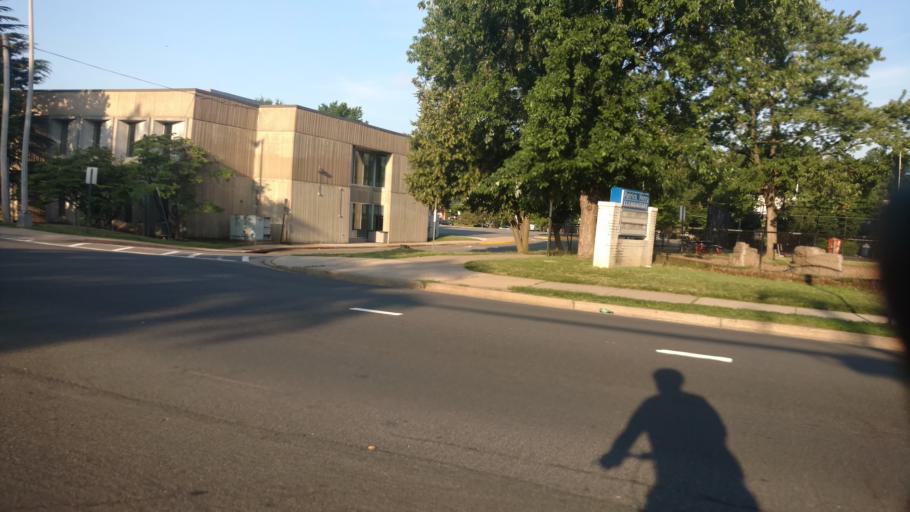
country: US
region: Virginia
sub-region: Arlington County
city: Arlington
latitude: 38.8658
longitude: -77.0877
